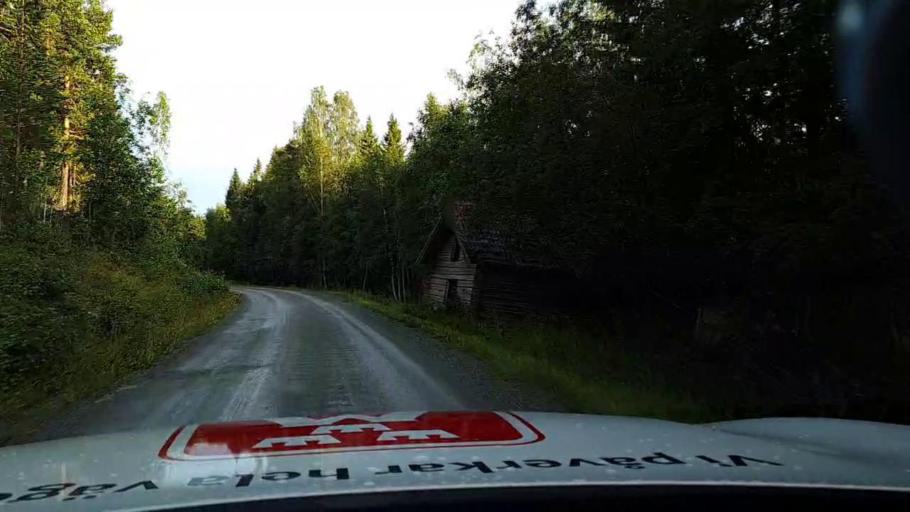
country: SE
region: Jaemtland
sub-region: Bergs Kommun
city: Hoverberg
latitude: 62.8624
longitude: 14.5306
